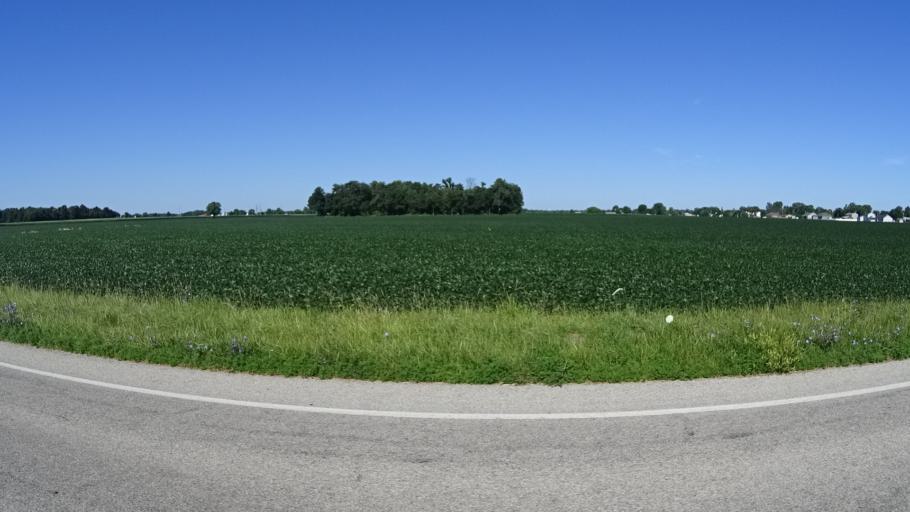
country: US
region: Ohio
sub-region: Erie County
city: Sandusky
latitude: 41.3935
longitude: -82.7193
